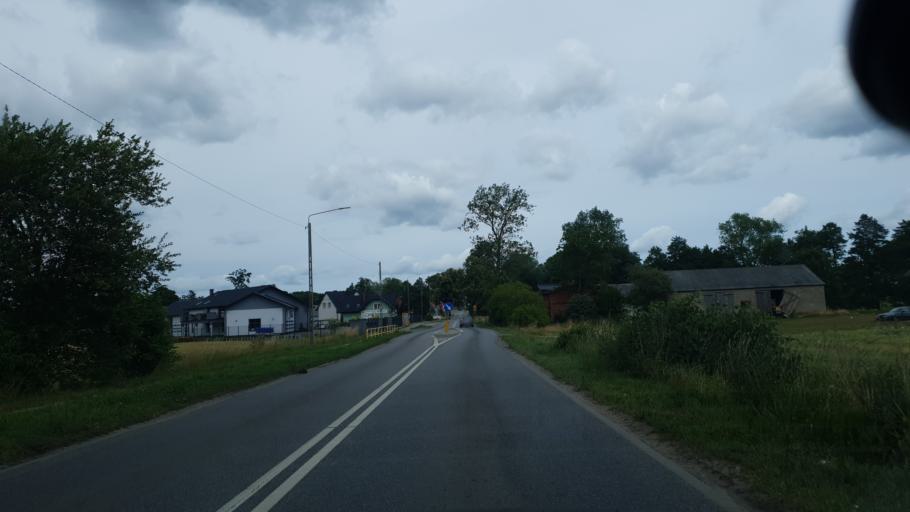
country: PL
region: Pomeranian Voivodeship
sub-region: Powiat kartuski
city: Przodkowo
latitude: 54.3780
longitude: 18.3100
